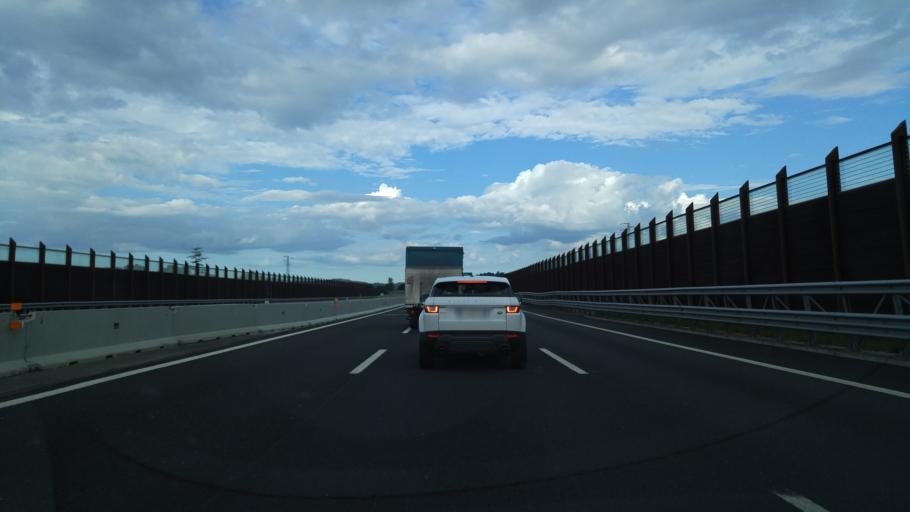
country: IT
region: Emilia-Romagna
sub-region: Provincia di Rimini
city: Montalbano
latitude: 43.9535
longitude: 12.7163
